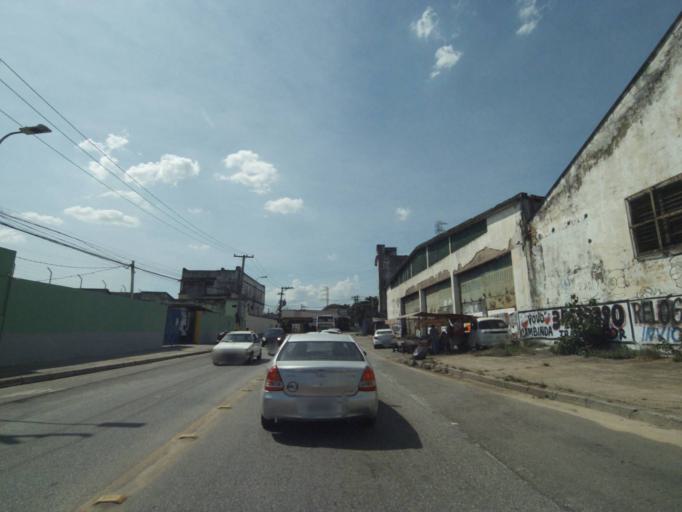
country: BR
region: Rio de Janeiro
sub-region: Sao Joao De Meriti
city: Sao Joao de Meriti
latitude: -22.8001
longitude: -43.3557
